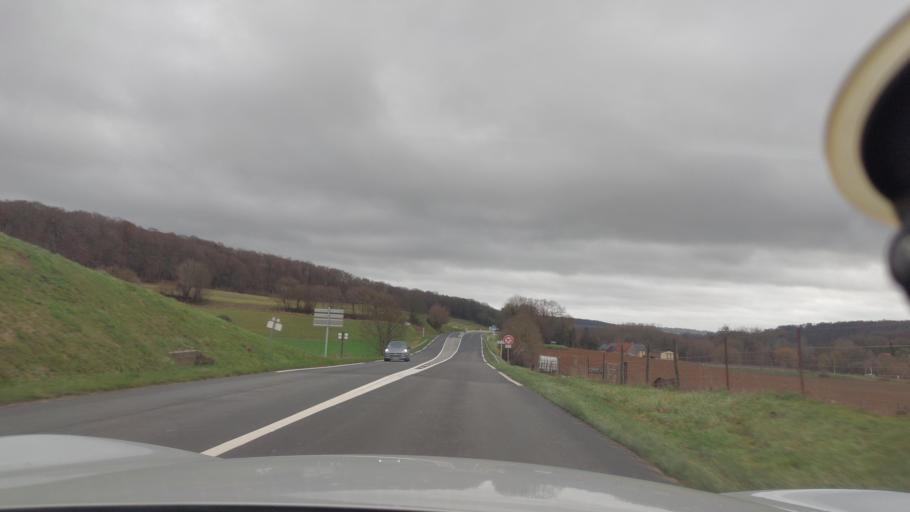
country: FR
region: Picardie
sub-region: Departement de l'Oise
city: Saint-Omer-en-Chaussee
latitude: 49.5693
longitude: 1.9616
